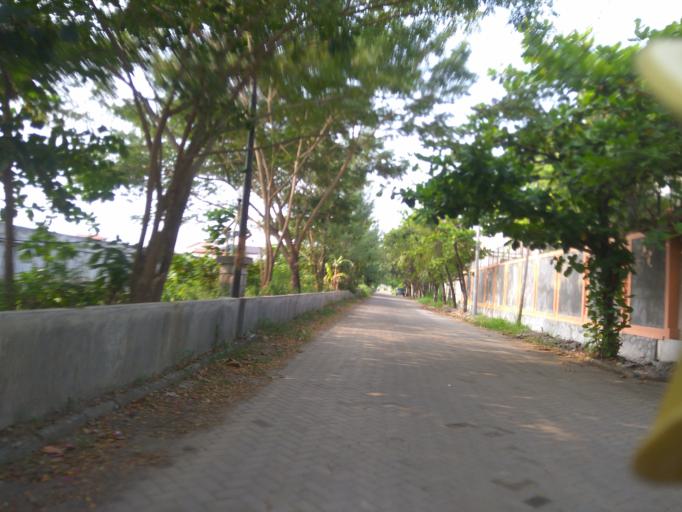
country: ID
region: Central Java
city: Semarang
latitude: -6.9677
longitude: 110.3944
